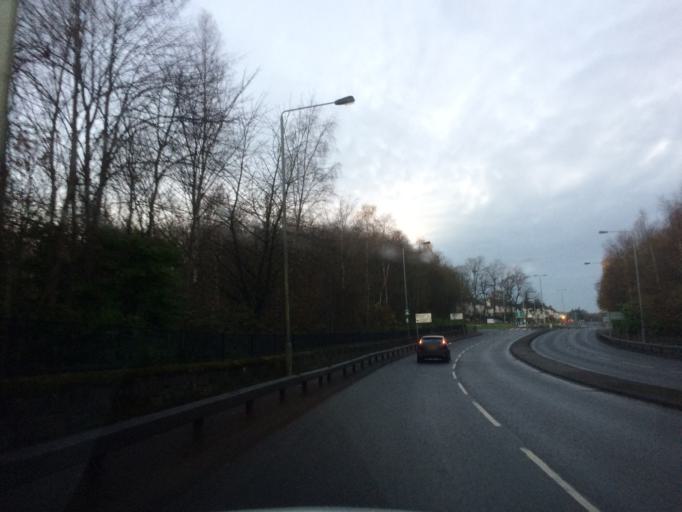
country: GB
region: Scotland
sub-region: East Renfrewshire
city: Giffnock
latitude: 55.8002
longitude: -4.3203
